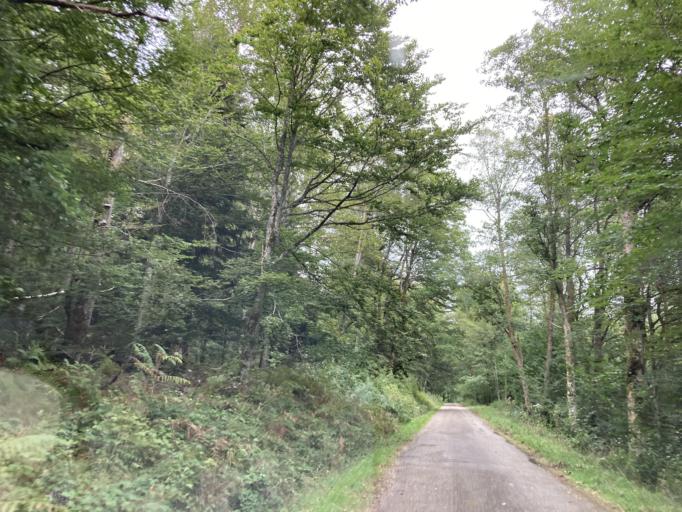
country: DE
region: Baden-Wuerttemberg
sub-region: Karlsruhe Region
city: Dobel
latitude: 48.7791
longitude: 8.5102
